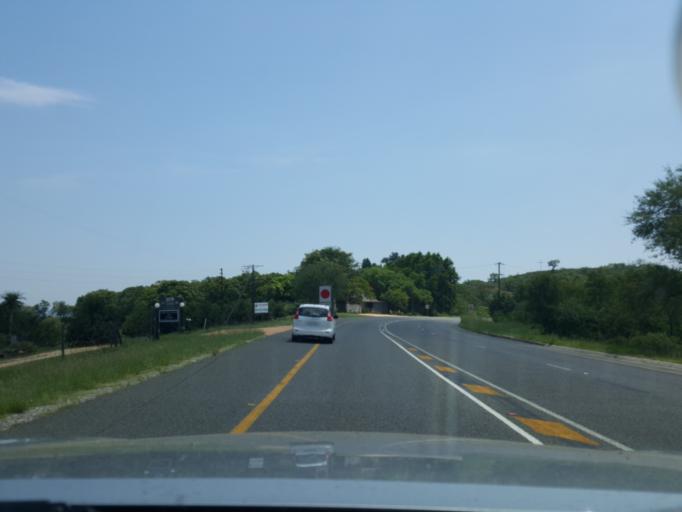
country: ZA
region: Mpumalanga
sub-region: Ehlanzeni District
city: White River
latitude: -25.0648
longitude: 31.1082
